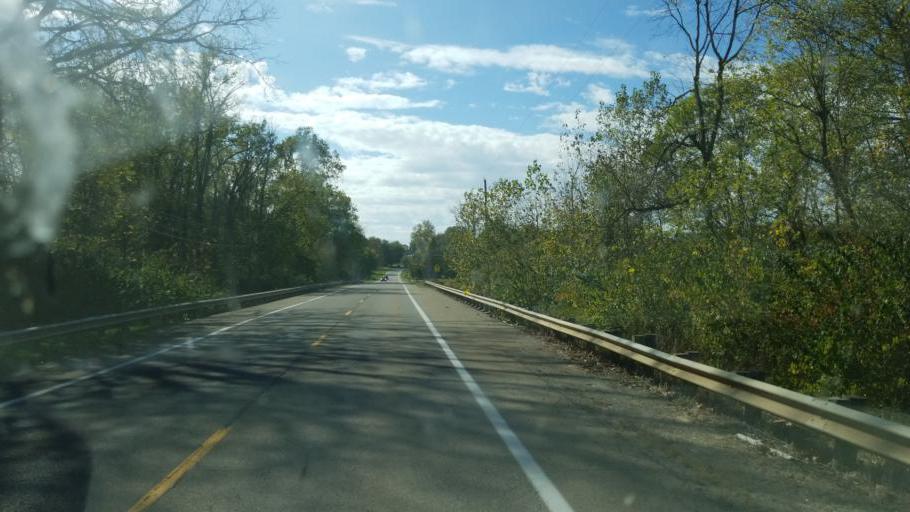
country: US
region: Ohio
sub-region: Morrow County
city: Mount Gilead
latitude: 40.5557
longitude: -82.8174
